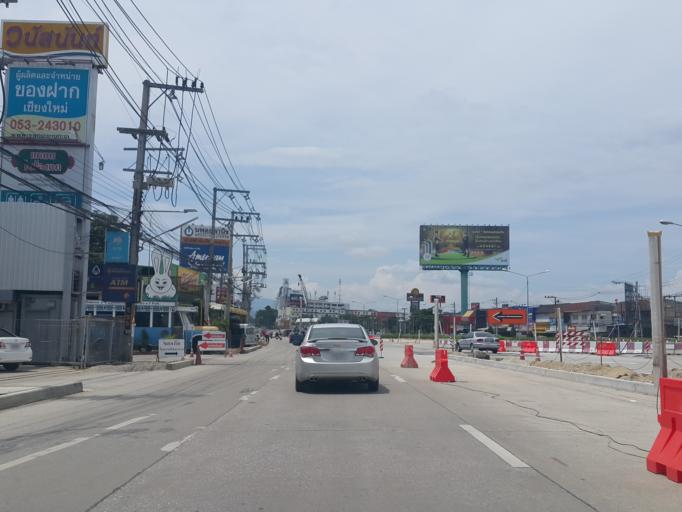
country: TH
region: Chiang Mai
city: Chiang Mai
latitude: 18.8073
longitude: 99.0154
